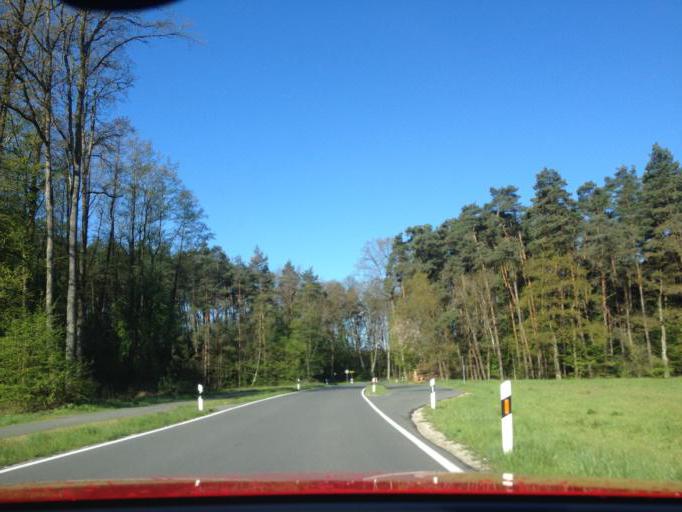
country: DE
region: Bavaria
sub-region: Regierungsbezirk Mittelfranken
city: Lauf an der Pegnitz
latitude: 49.4822
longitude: 11.2804
